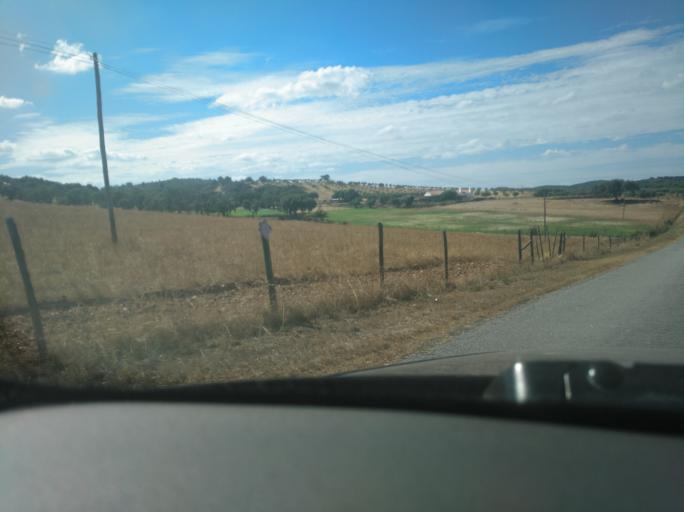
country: ES
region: Extremadura
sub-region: Provincia de Badajoz
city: La Codosera
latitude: 39.1491
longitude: -7.1581
